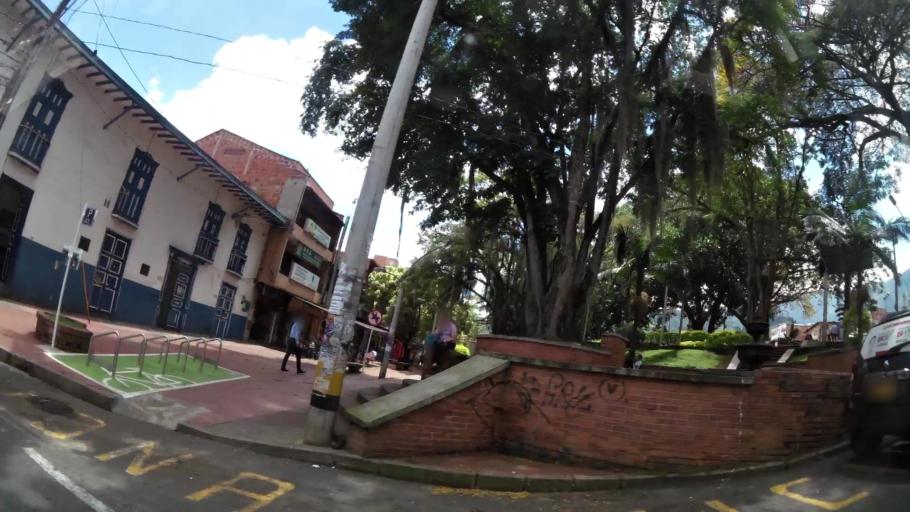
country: CO
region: Antioquia
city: La Estrella
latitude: 6.1579
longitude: -75.6431
